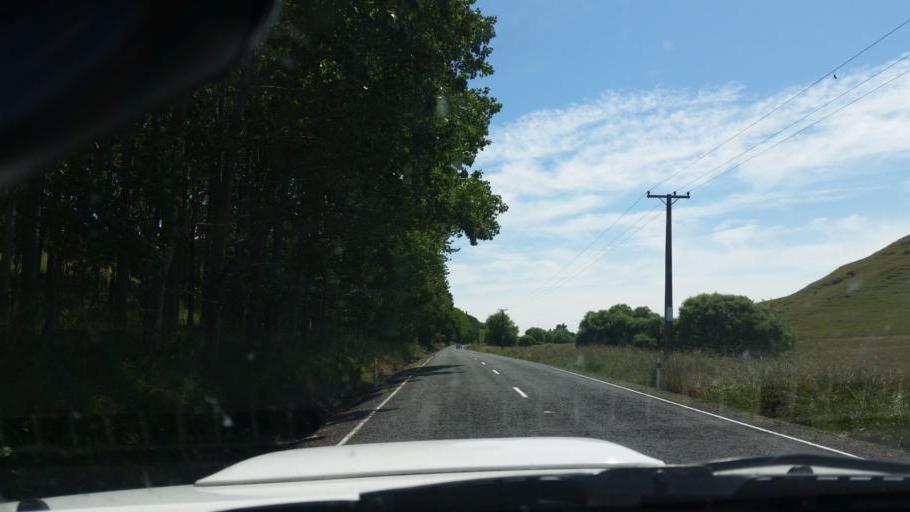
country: NZ
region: Auckland
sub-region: Auckland
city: Wellsford
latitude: -36.1951
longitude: 174.3990
